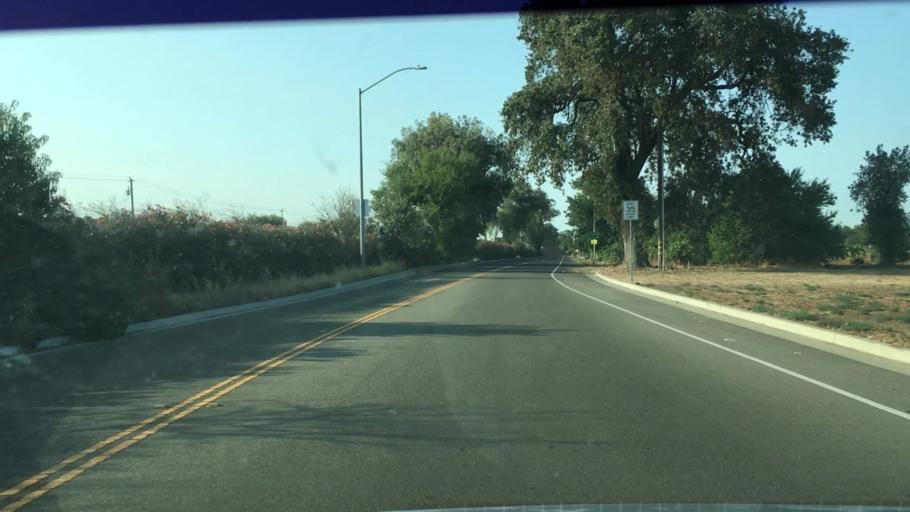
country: US
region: California
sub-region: San Joaquin County
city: Lodi
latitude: 38.0946
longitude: -121.2605
